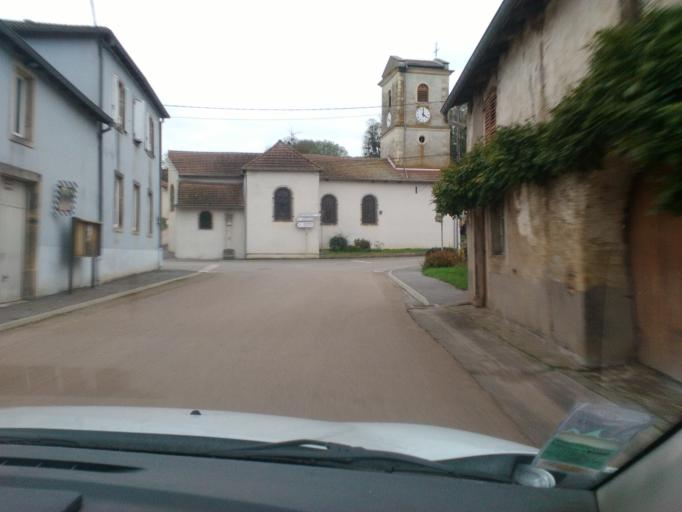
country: FR
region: Lorraine
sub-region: Departement des Vosges
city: Mirecourt
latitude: 48.3124
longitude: 6.2084
